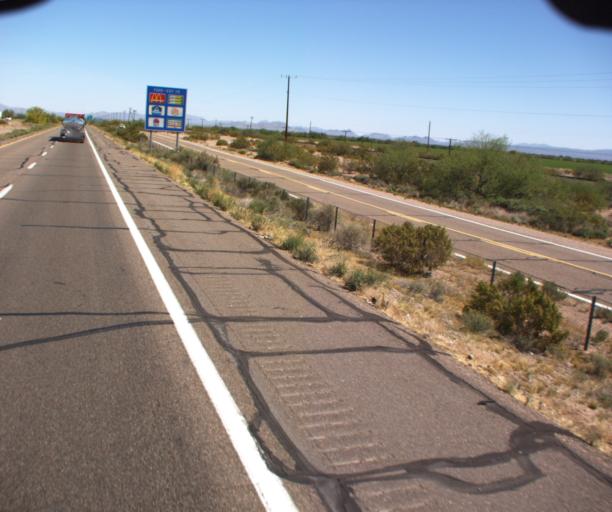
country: US
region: Arizona
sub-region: Maricopa County
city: Gila Bend
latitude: 32.9356
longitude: -112.7791
